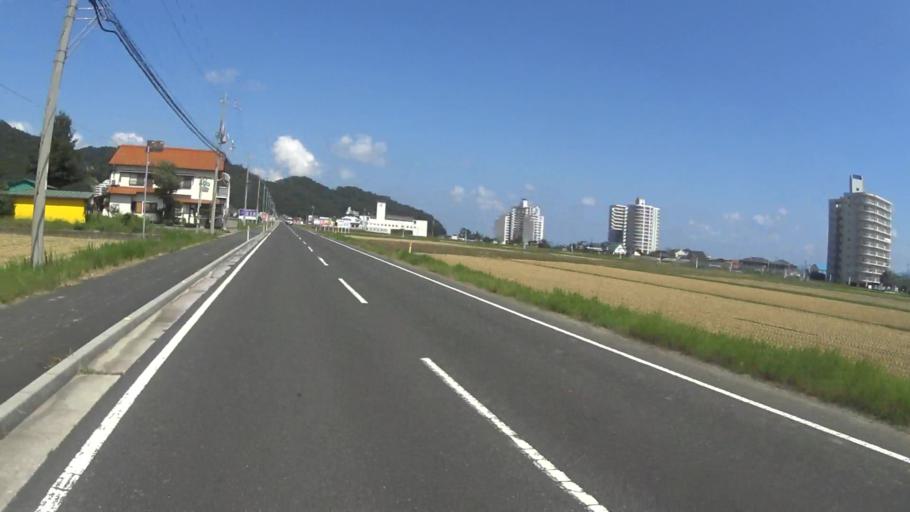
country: JP
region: Kyoto
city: Miyazu
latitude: 35.6102
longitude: 135.2273
